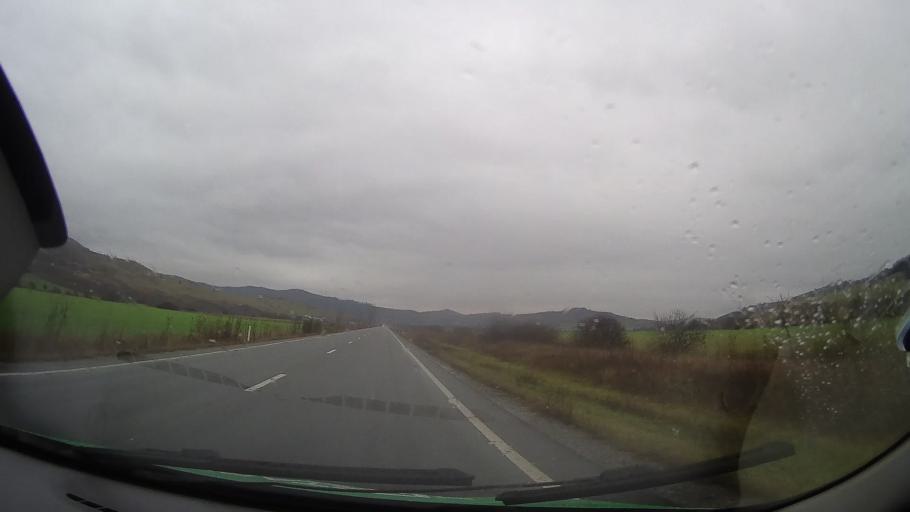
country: RO
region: Bistrita-Nasaud
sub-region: Comuna Teaca
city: Teaca
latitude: 46.9268
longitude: 24.4855
